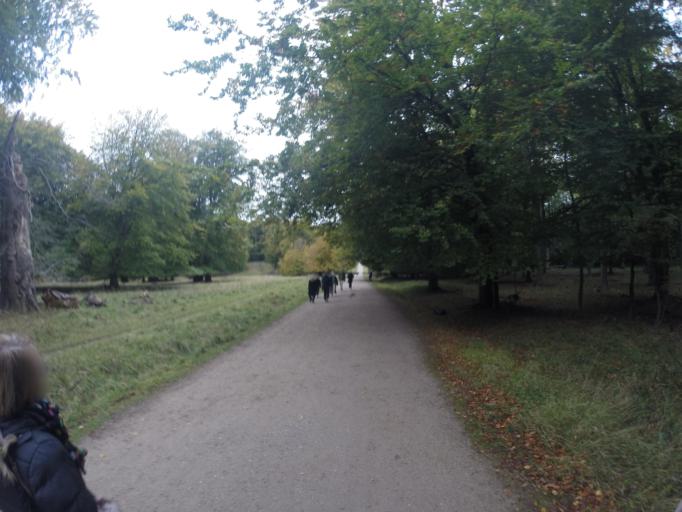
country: DK
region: Capital Region
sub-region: Gentofte Kommune
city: Charlottenlund
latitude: 55.7757
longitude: 12.5550
